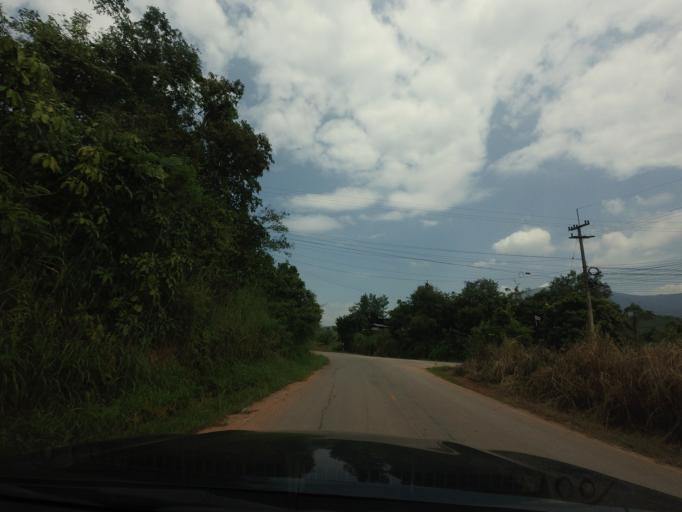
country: TH
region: Uttaradit
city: Fak Tha
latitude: 17.8155
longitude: 100.9386
